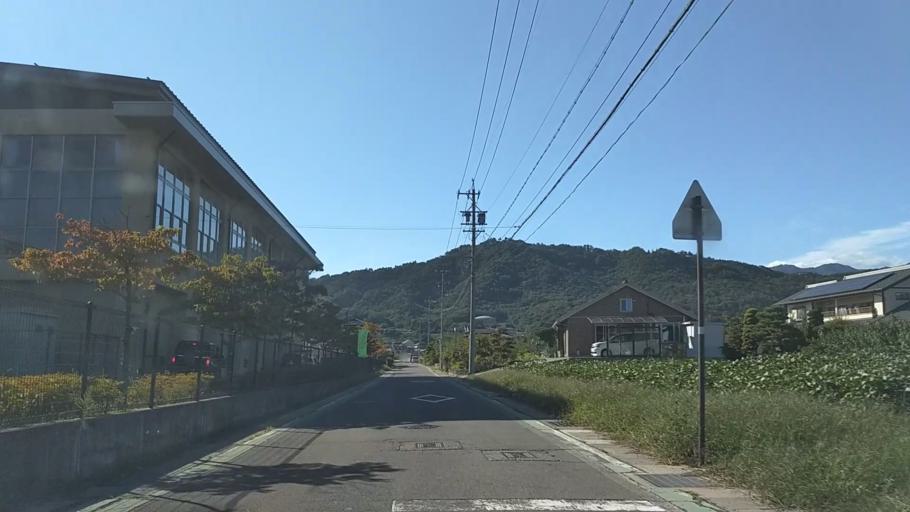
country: JP
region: Nagano
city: Nagano-shi
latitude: 36.6005
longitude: 138.1369
